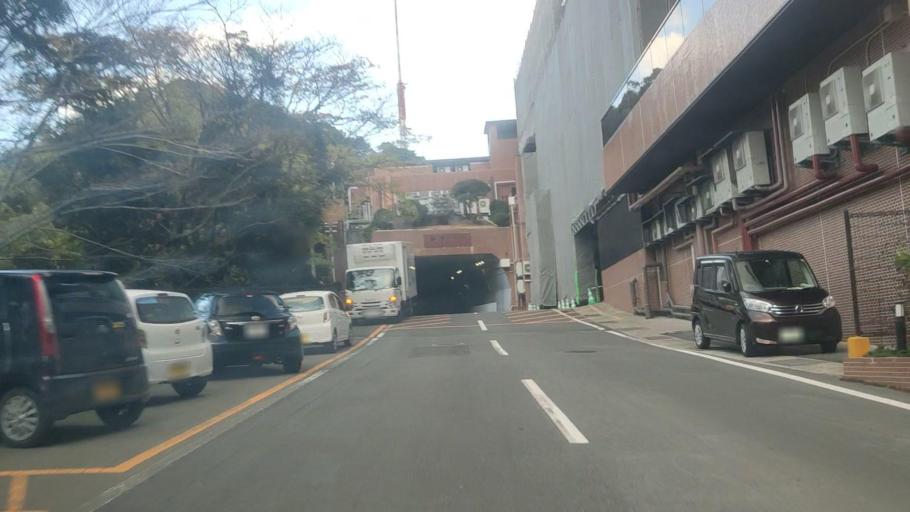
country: JP
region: Kagoshima
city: Kagoshima-shi
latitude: 31.5949
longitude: 130.5469
